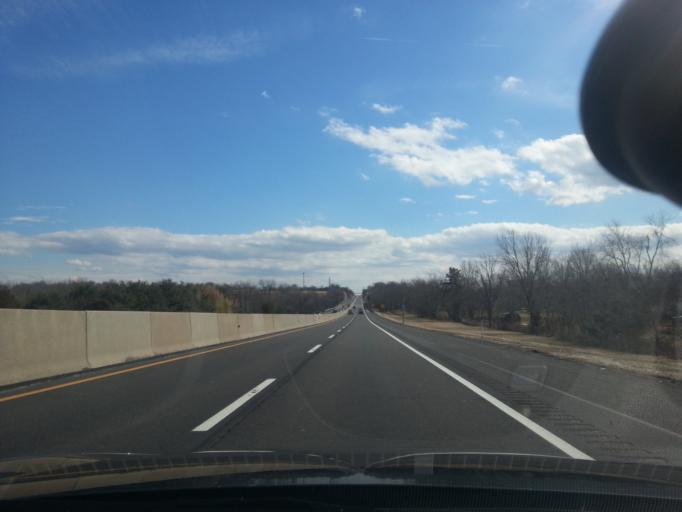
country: US
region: Pennsylvania
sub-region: Montgomery County
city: Harleysville
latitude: 40.3316
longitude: -75.3814
